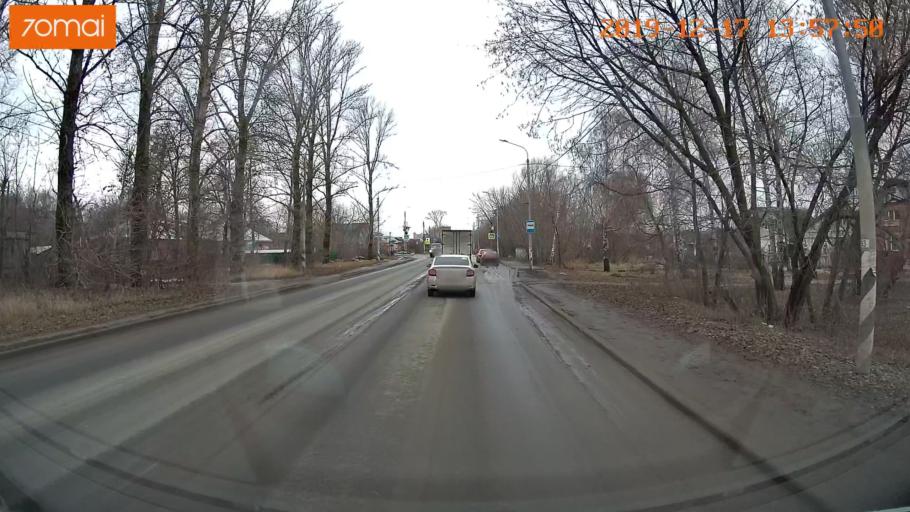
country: RU
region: Rjazan
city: Ryazan'
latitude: 54.6249
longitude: 39.6885
